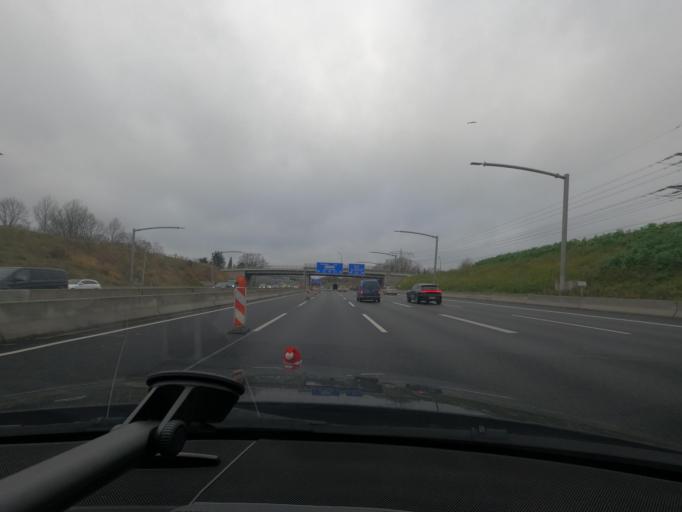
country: DE
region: Hamburg
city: Eidelstedt
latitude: 53.6075
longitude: 9.9150
